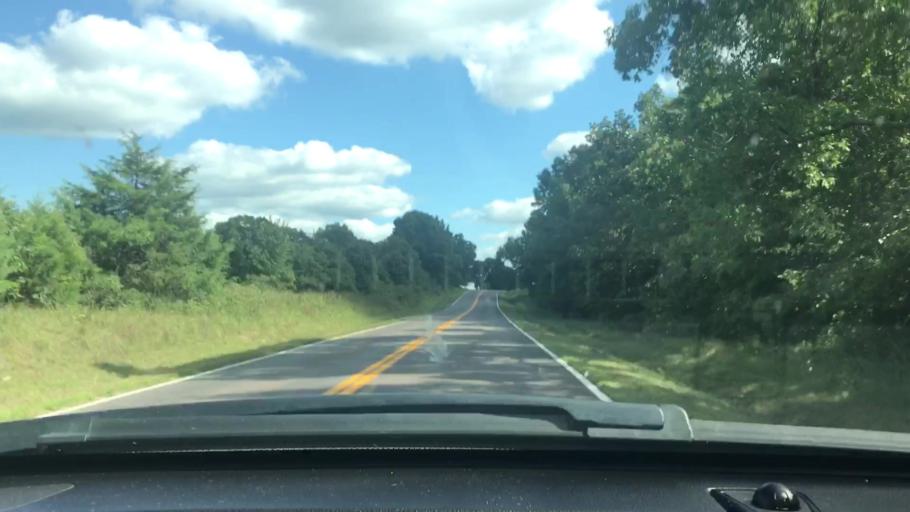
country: US
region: Missouri
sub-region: Wright County
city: Hartville
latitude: 37.3630
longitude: -92.3457
